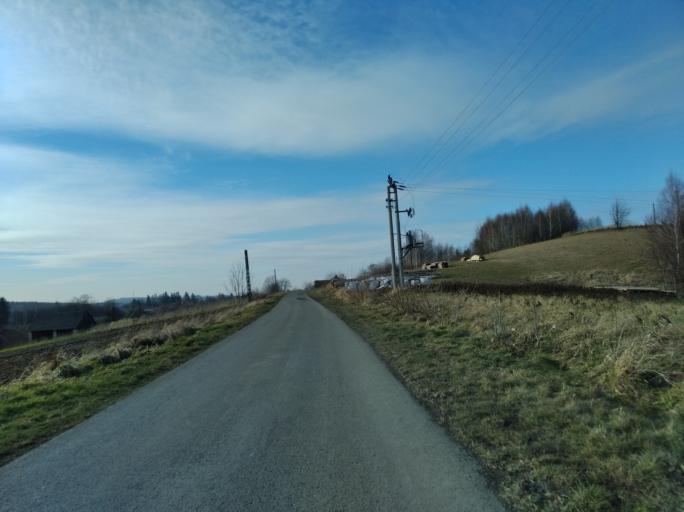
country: PL
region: Subcarpathian Voivodeship
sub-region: Powiat strzyzowski
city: Gwoznica Gorna
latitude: 49.8266
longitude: 21.9718
